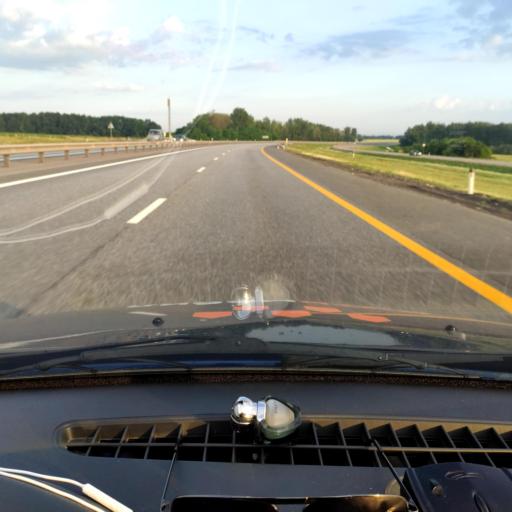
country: RU
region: Lipetsk
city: Zadonsk
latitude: 52.4430
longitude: 38.7909
